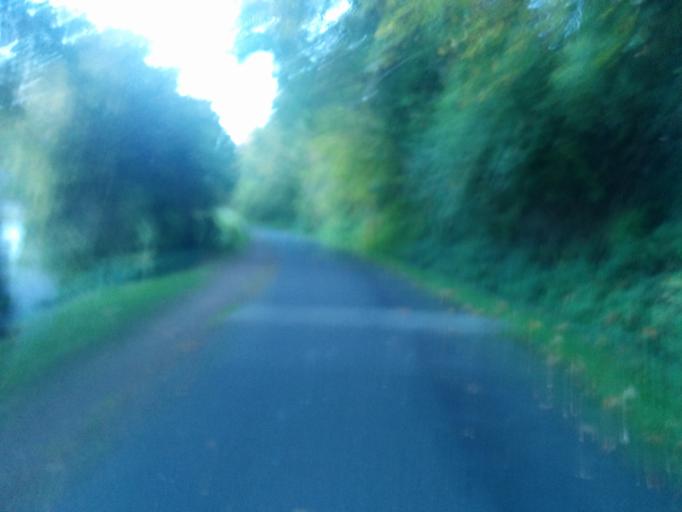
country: US
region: Washington
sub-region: King County
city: Lake Forest Park
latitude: 47.7206
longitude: -122.2813
